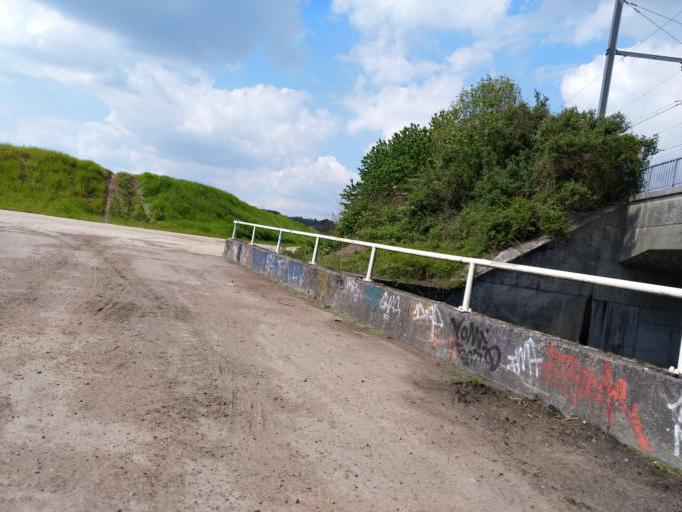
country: BE
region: Wallonia
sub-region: Province du Hainaut
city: Mons
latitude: 50.4712
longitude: 3.9486
